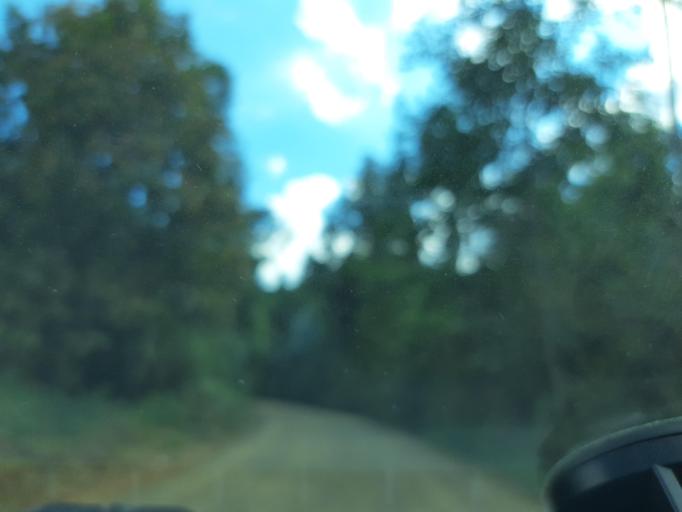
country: CO
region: Boyaca
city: Raquira
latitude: 5.5367
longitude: -73.6593
